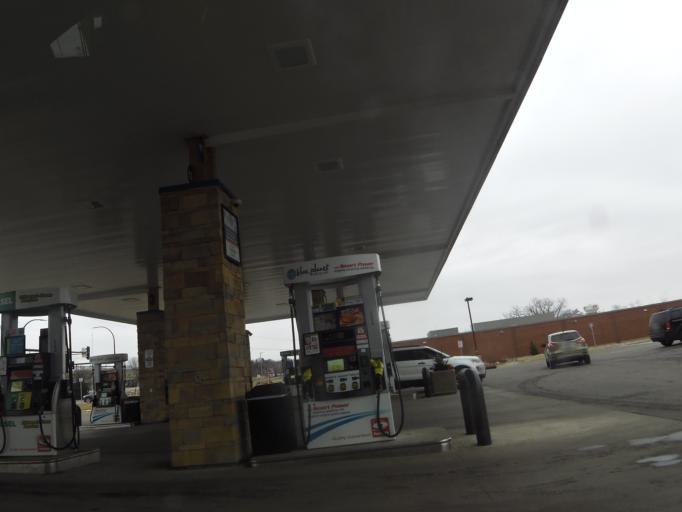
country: US
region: Minnesota
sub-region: Carver County
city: Waconia
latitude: 44.8395
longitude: -93.7955
